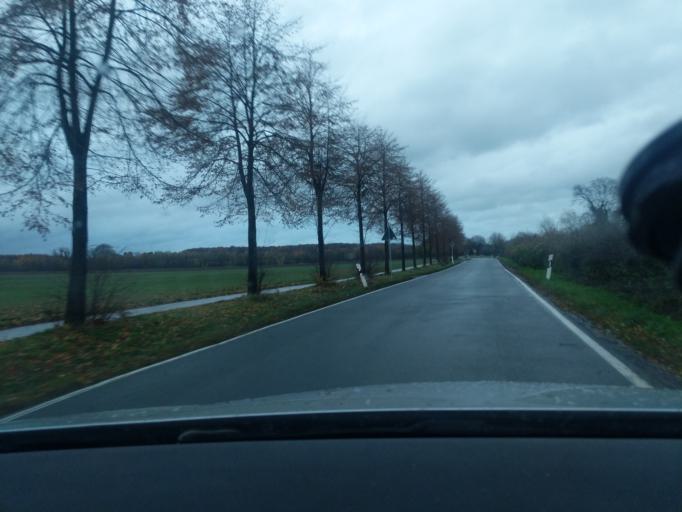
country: DE
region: North Rhine-Westphalia
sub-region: Regierungsbezirk Arnsberg
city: Bonen
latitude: 51.5839
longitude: 7.7799
